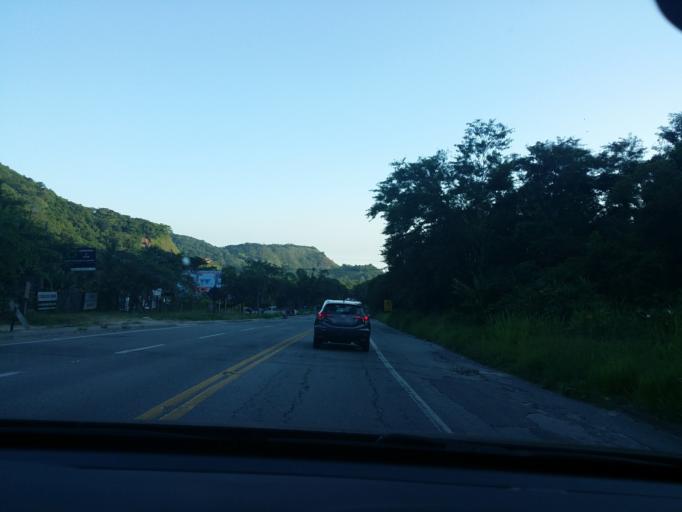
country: BR
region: Sao Paulo
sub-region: Sao Sebastiao
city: Sao Sebastiao
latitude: -23.7519
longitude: -45.7256
